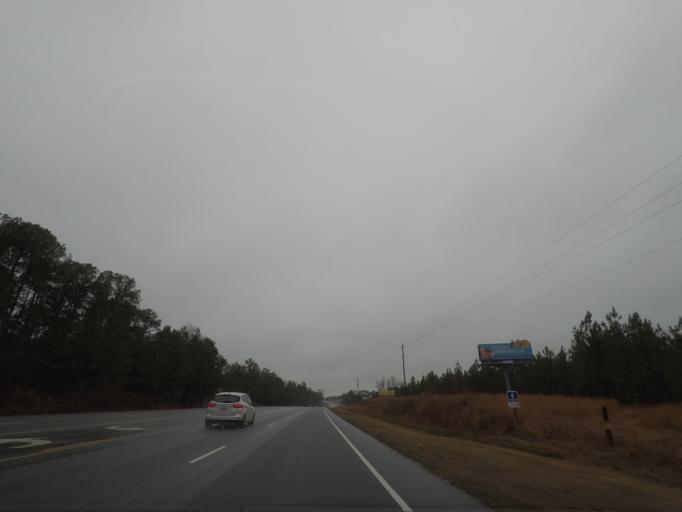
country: US
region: North Carolina
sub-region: Lee County
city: Broadway
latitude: 35.3538
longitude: -79.1092
